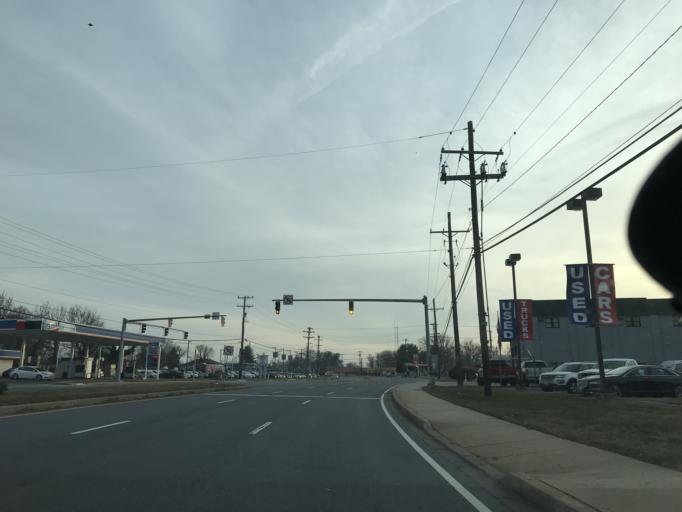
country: US
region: Maryland
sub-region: Prince George's County
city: Woodlawn
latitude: 38.9524
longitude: -76.8830
